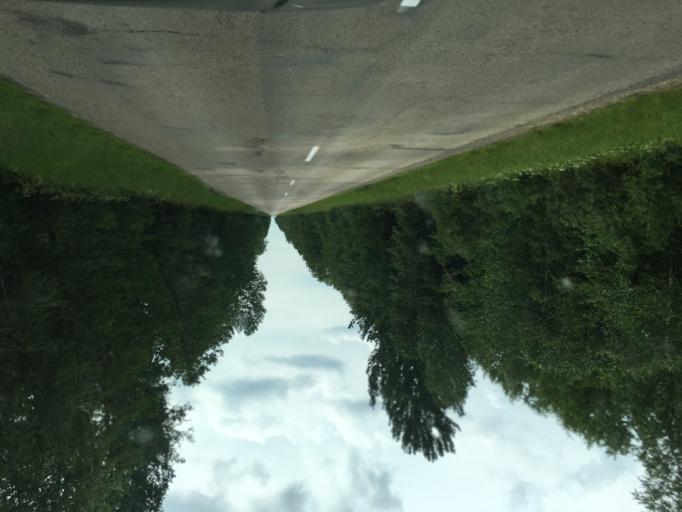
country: LV
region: Rugaju
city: Rugaji
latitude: 56.7969
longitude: 27.0992
